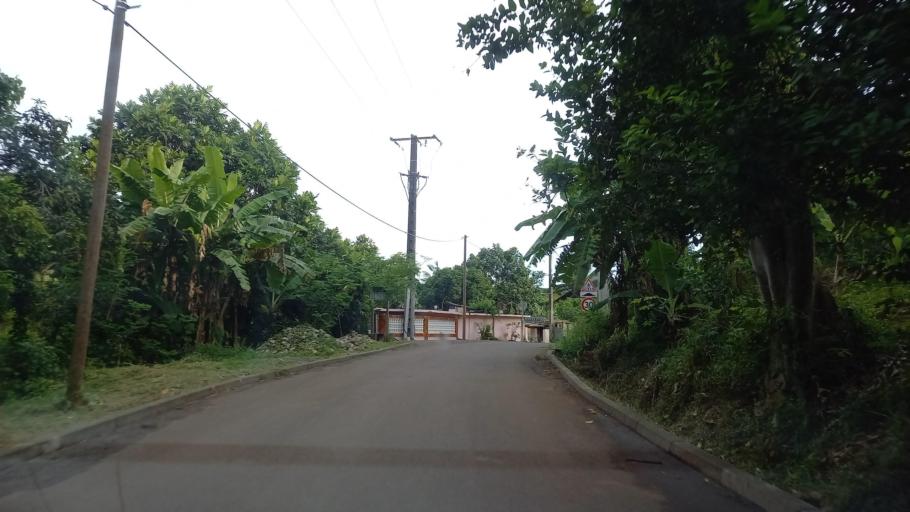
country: YT
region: Acoua
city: Acoua
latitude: -12.7476
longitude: 45.0564
